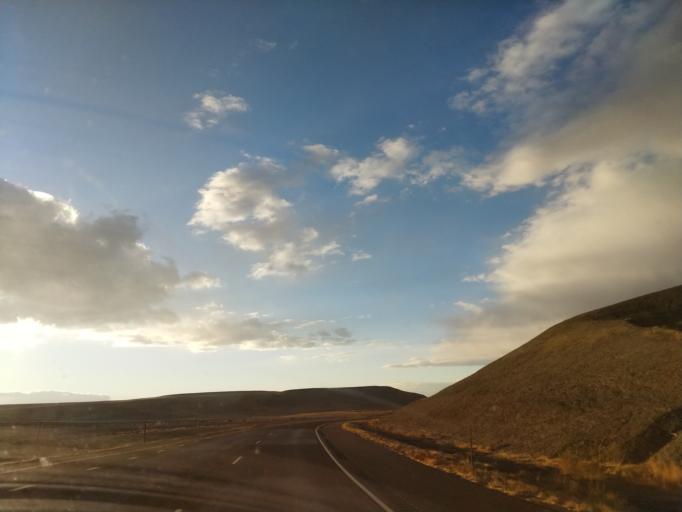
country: US
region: Colorado
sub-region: Delta County
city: Delta
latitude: 38.7514
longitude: -108.1619
